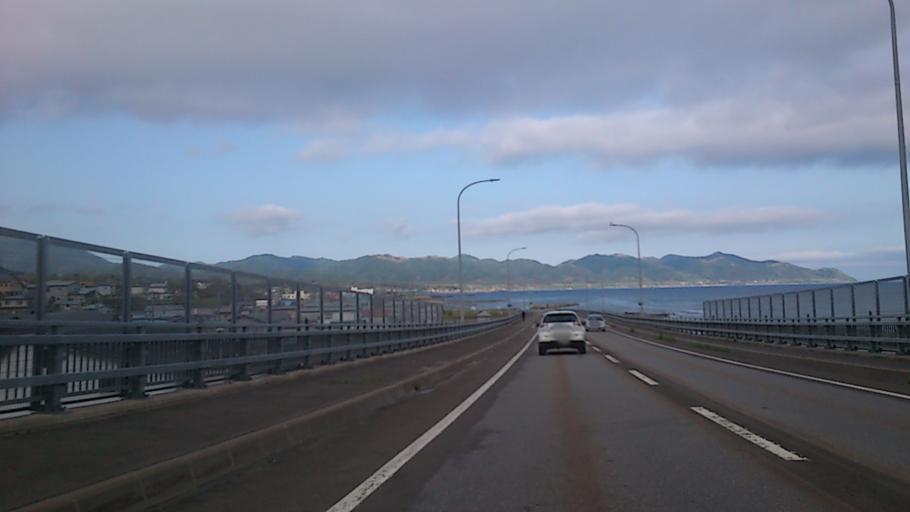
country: JP
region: Aomori
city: Shimokizukuri
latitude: 41.4246
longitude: 140.0917
